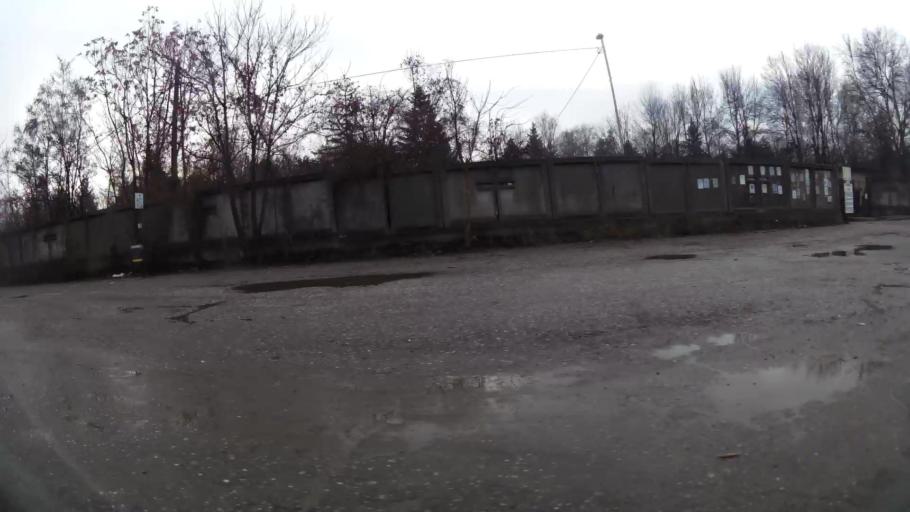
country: BG
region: Sofia-Capital
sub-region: Stolichna Obshtina
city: Sofia
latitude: 42.7203
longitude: 23.3629
